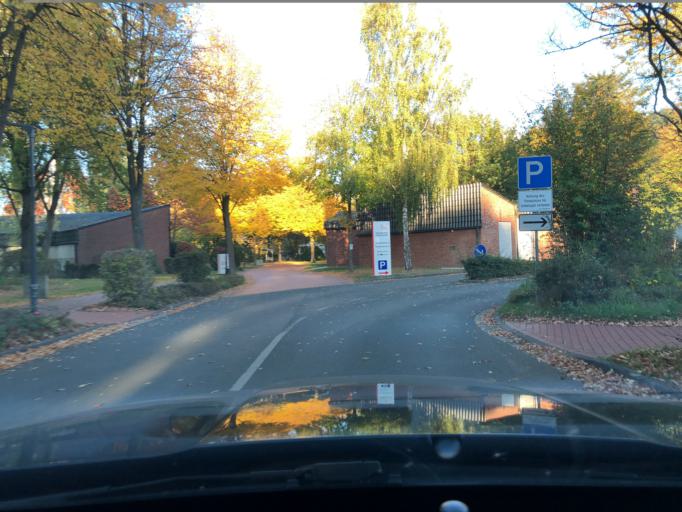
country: DE
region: North Rhine-Westphalia
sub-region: Regierungsbezirk Munster
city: Telgte
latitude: 52.0122
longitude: 7.7084
